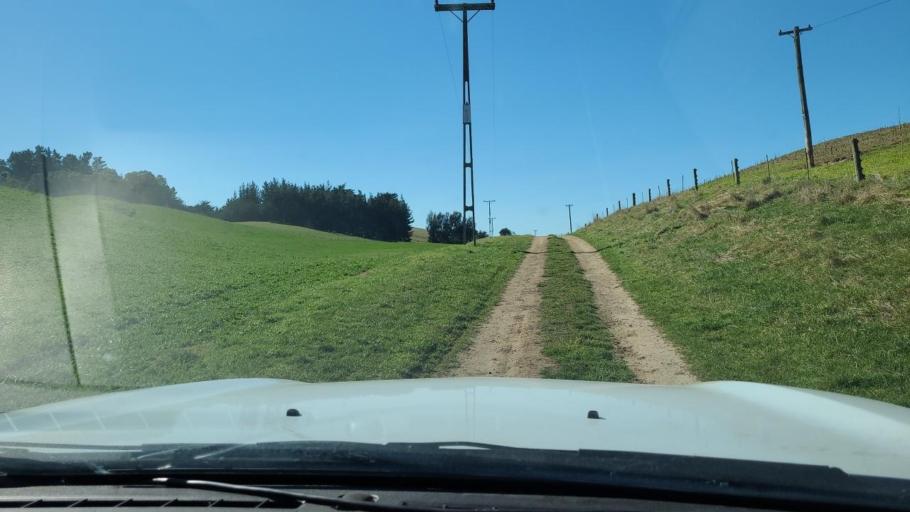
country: NZ
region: Hawke's Bay
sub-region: Hastings District
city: Hastings
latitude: -39.7938
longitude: 176.6522
